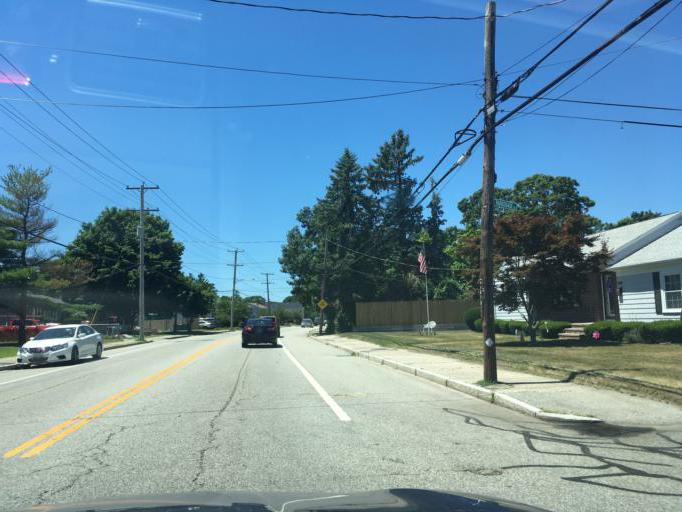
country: US
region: Rhode Island
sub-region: Kent County
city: Warwick
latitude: 41.7007
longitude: -71.3892
